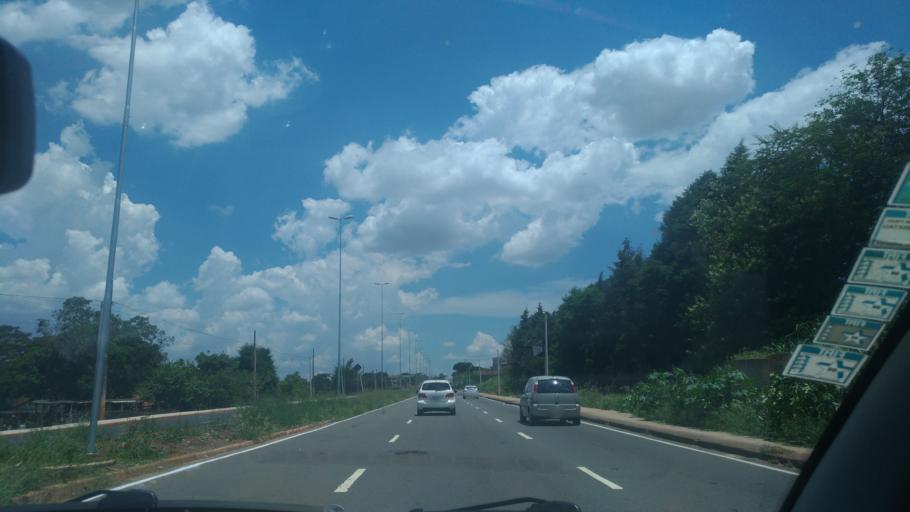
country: BR
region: Sao Paulo
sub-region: Nova Odessa
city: Nova Odessa
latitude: -22.7655
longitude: -47.3189
